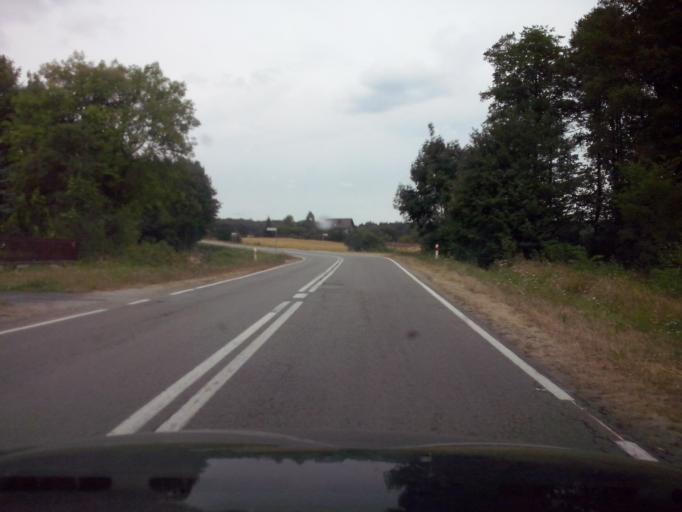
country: PL
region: Swietokrzyskie
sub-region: Powiat kielecki
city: Rakow
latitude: 50.7110
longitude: 21.0592
